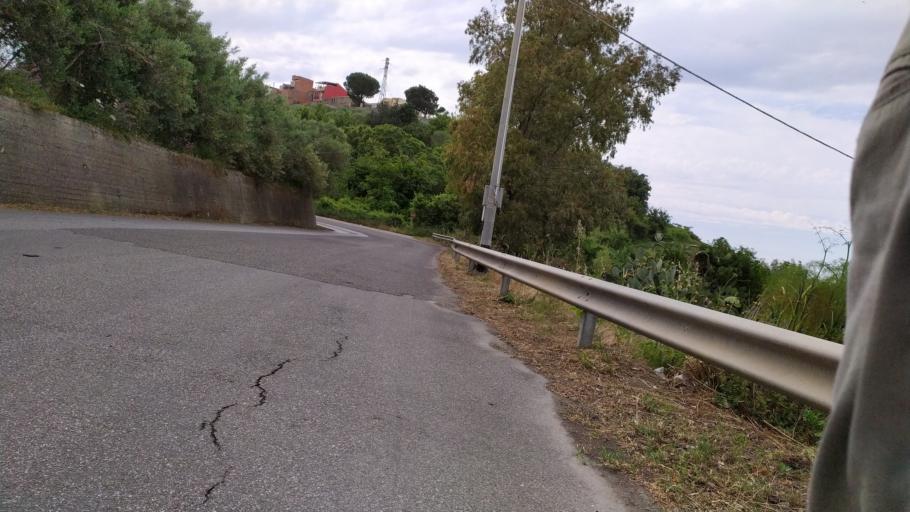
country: IT
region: Sicily
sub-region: Messina
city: San Filippo del Mela
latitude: 38.1690
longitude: 15.2808
